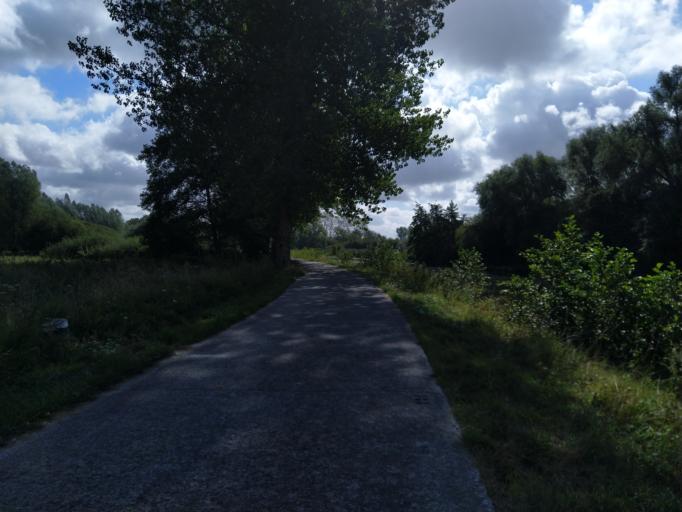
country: BE
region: Wallonia
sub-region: Province du Hainaut
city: Merbes-le-Chateau
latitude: 50.3194
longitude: 4.1688
